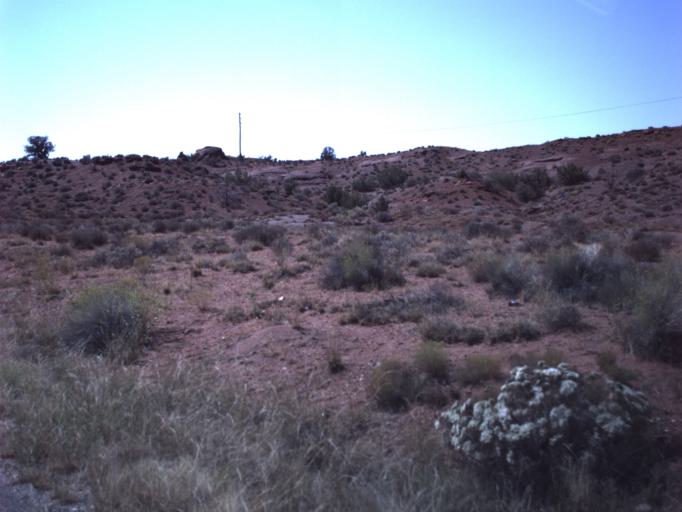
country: US
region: Utah
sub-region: Grand County
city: Moab
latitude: 38.7427
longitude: -109.3313
